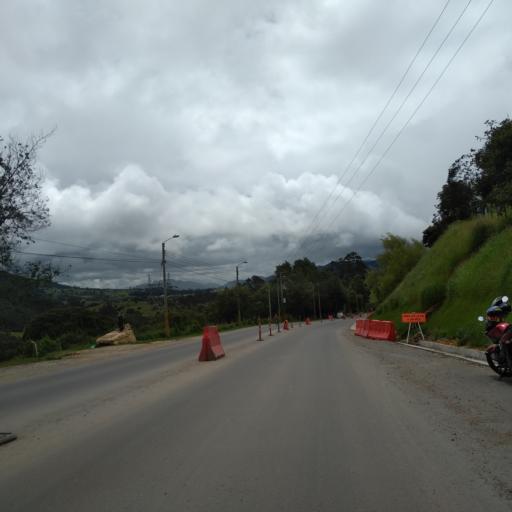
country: CO
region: Cundinamarca
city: La Calera
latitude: 4.6993
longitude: -73.9829
